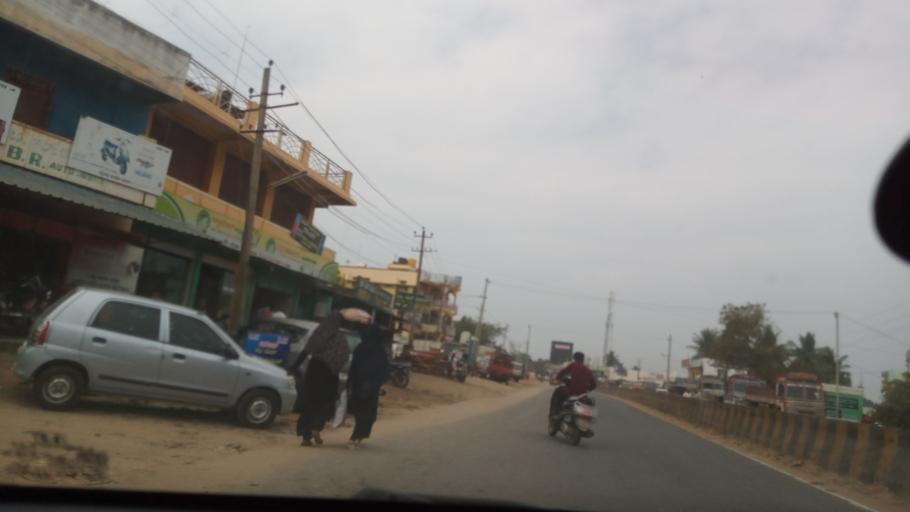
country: IN
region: Karnataka
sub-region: Chamrajnagar
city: Chamrajnagar
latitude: 11.9150
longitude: 76.9426
